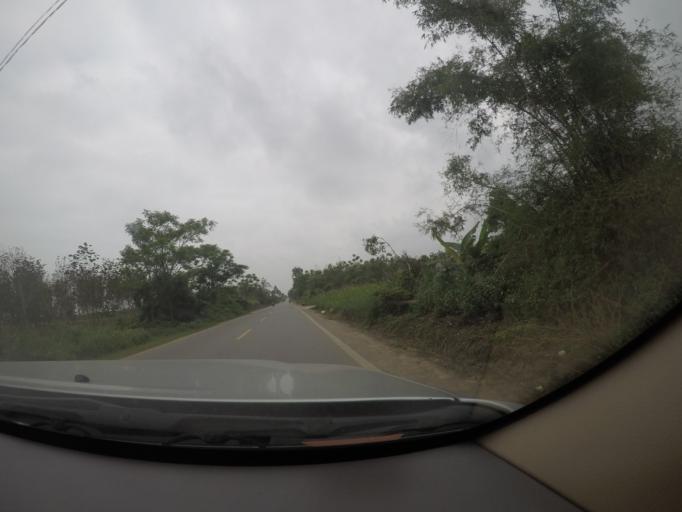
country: VN
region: Quang Binh
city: Hoan Lao
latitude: 17.5355
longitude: 106.4712
